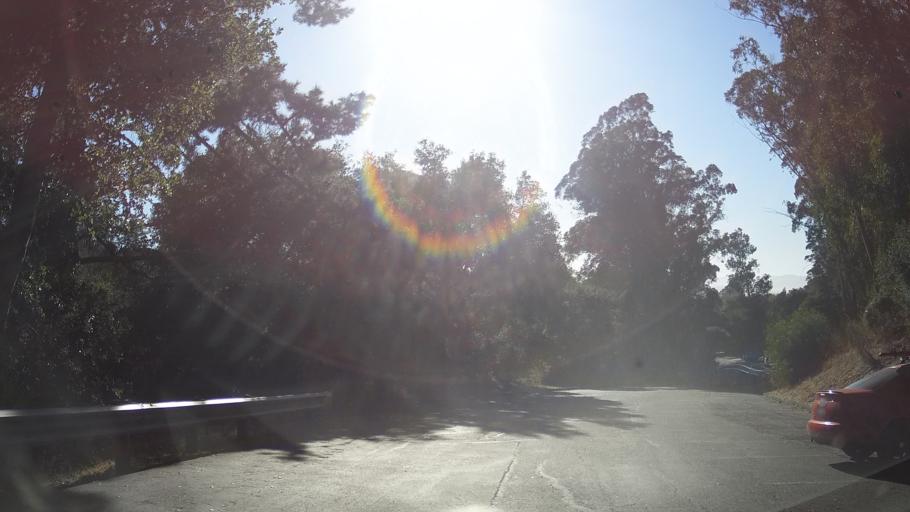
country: US
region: California
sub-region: Contra Costa County
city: East Richmond Heights
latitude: 37.9519
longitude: -122.3164
